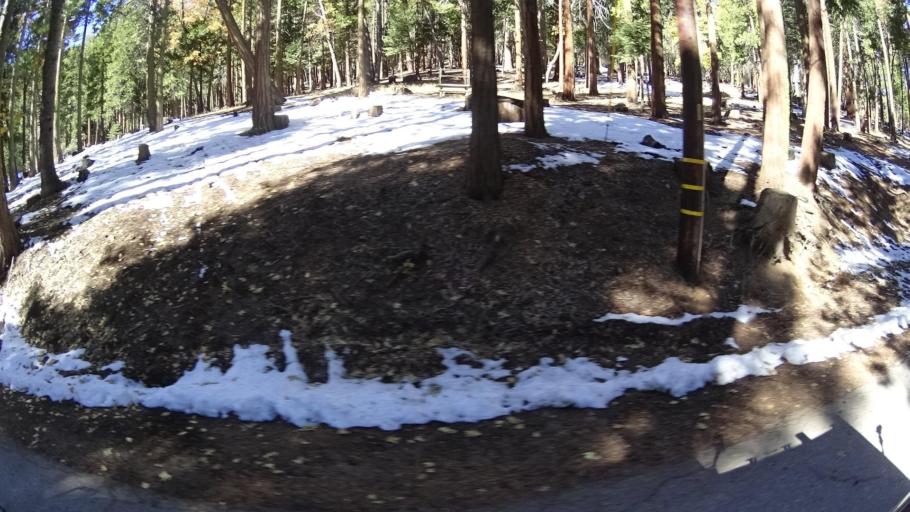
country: US
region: California
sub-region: Kern County
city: Alta Sierra
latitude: 35.7331
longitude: -118.5538
